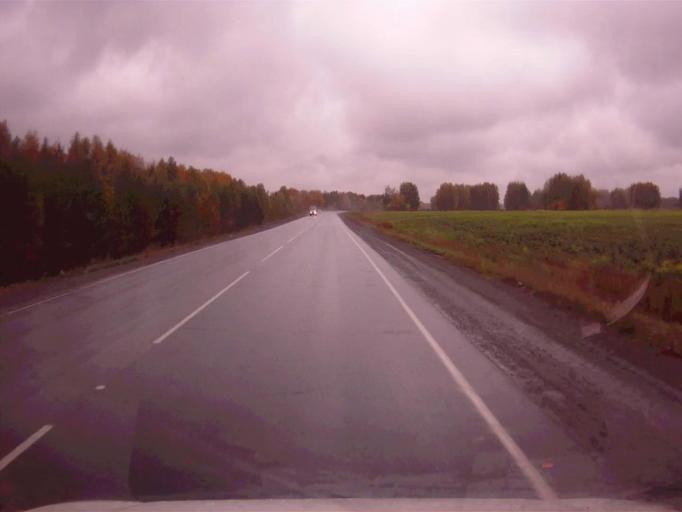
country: RU
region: Chelyabinsk
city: Roshchino
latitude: 55.3989
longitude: 61.0805
